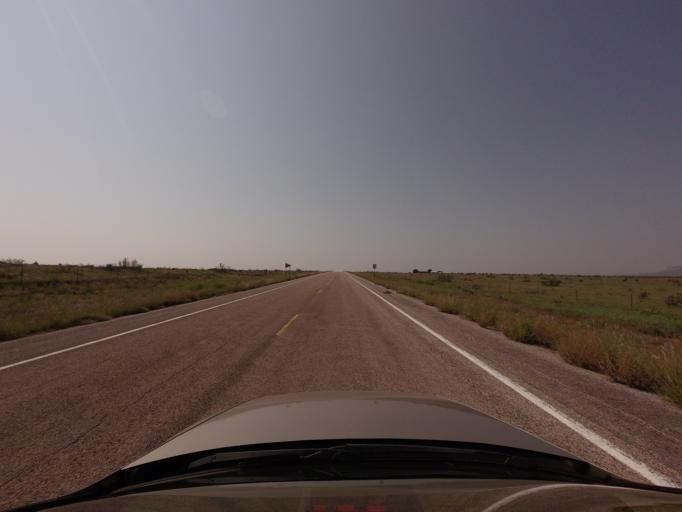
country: US
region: New Mexico
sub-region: Quay County
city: Tucumcari
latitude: 34.9586
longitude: -103.7571
